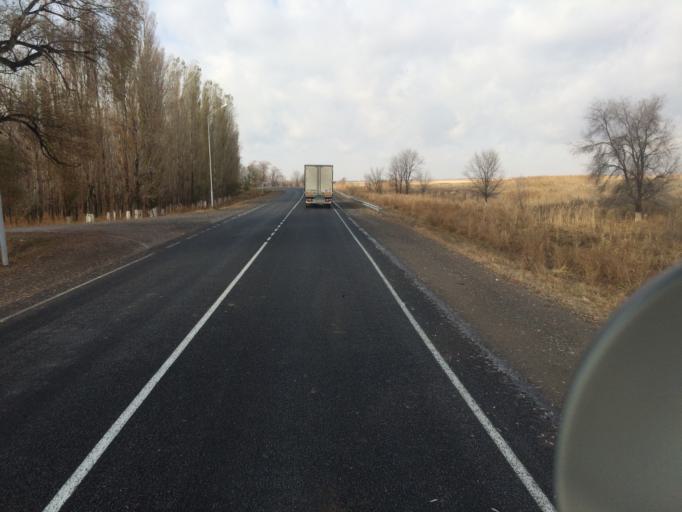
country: KZ
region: Zhambyl
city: Georgiyevka
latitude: 43.2222
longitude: 74.4505
